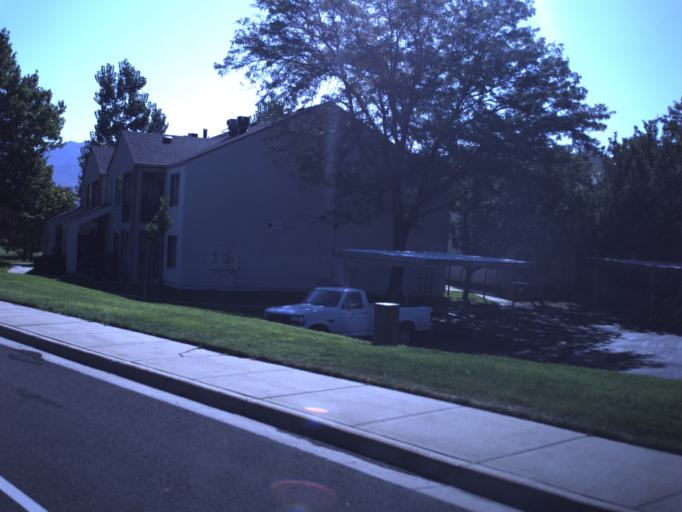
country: US
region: Utah
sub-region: Salt Lake County
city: Taylorsville
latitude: 40.6681
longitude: -111.9331
